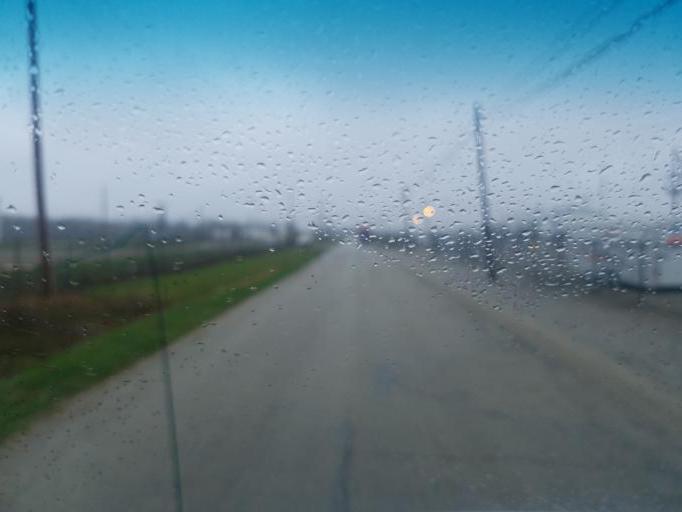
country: US
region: Ohio
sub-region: Wood County
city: North Baltimore
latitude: 41.2292
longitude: -83.6403
